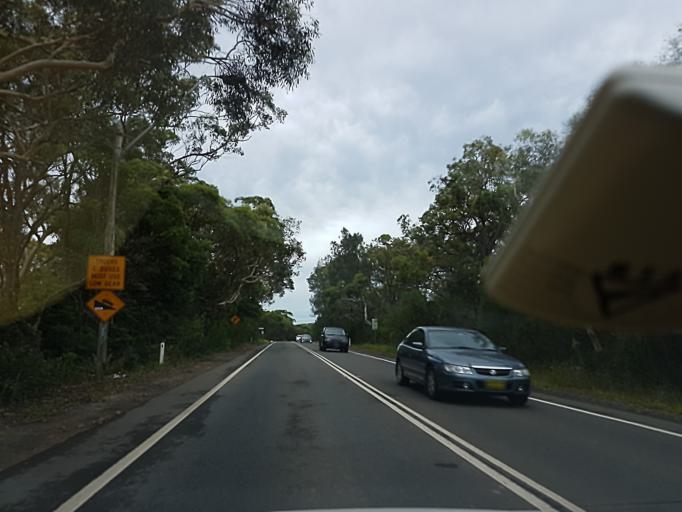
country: AU
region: New South Wales
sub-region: Warringah
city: Allambie Heights
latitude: -33.7361
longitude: 151.2452
